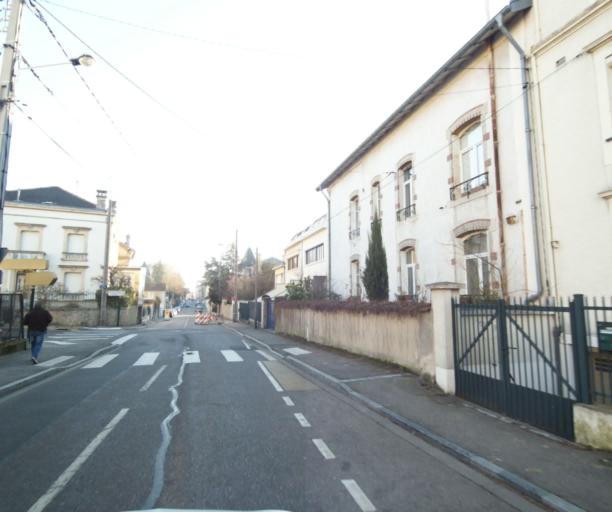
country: FR
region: Lorraine
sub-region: Departement de Meurthe-et-Moselle
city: Laxou
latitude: 48.6872
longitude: 6.1554
